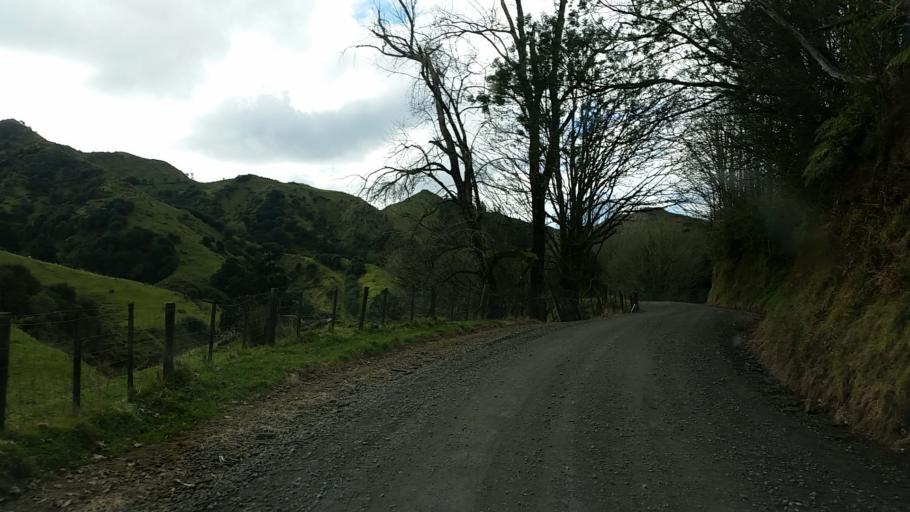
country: NZ
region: Taranaki
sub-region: New Plymouth District
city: Waitara
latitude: -39.1635
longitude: 174.5733
